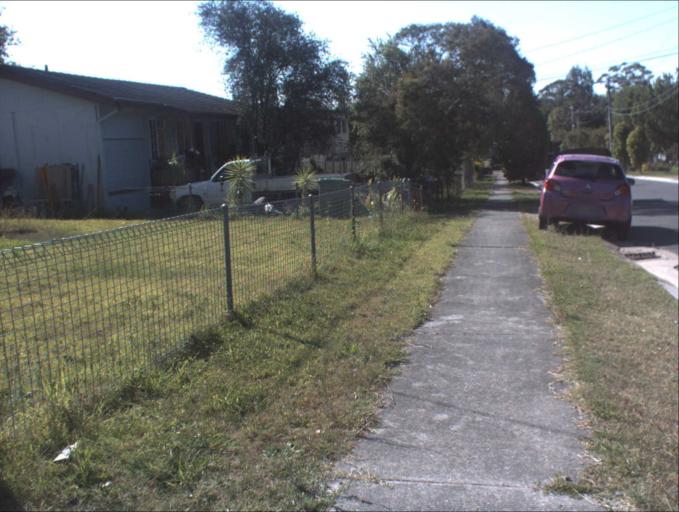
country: AU
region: Queensland
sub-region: Logan
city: Logan City
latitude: -27.6559
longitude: 153.1095
